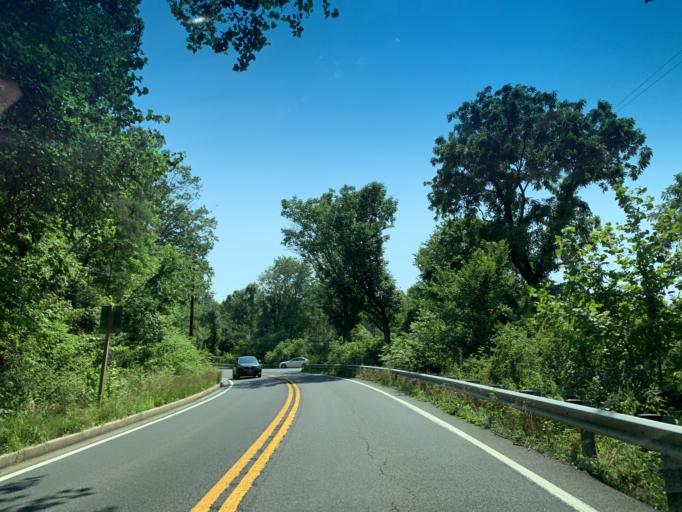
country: US
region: Maryland
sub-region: Frederick County
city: Urbana
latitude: 39.2640
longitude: -77.3437
